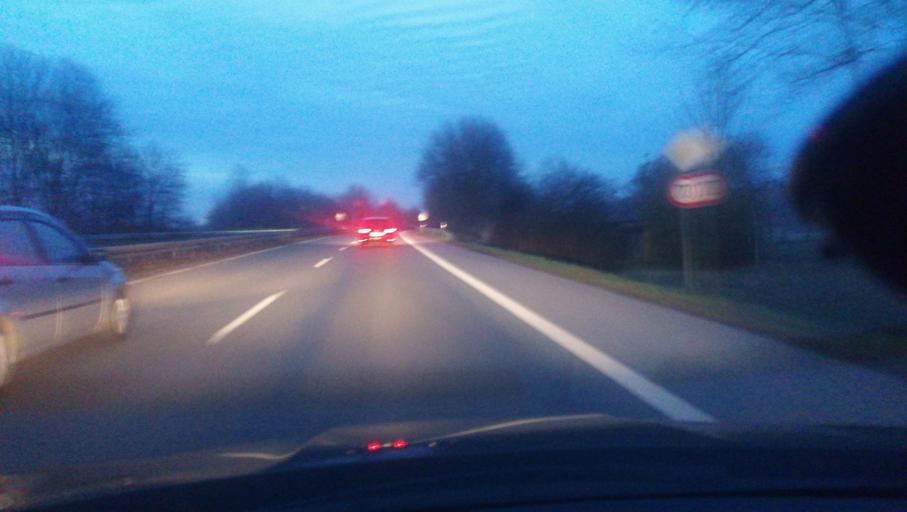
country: DE
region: North Rhine-Westphalia
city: Waltrop
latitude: 51.5495
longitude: 7.4012
